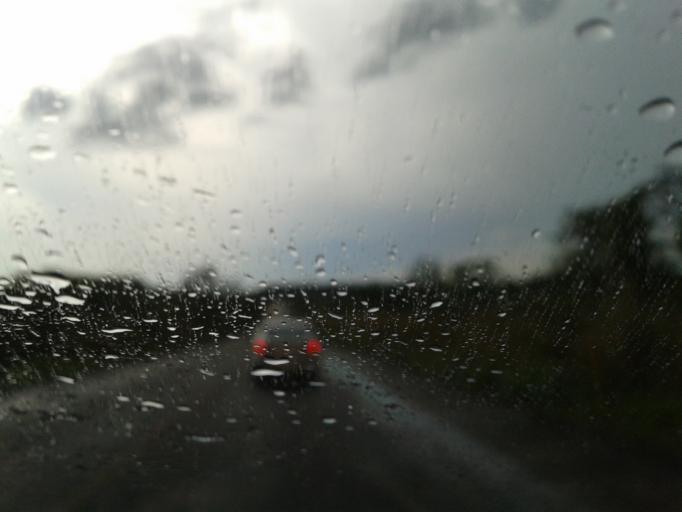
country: BR
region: Goias
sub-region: Quirinopolis
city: Quirinopolis
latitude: -18.3396
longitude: -50.4172
